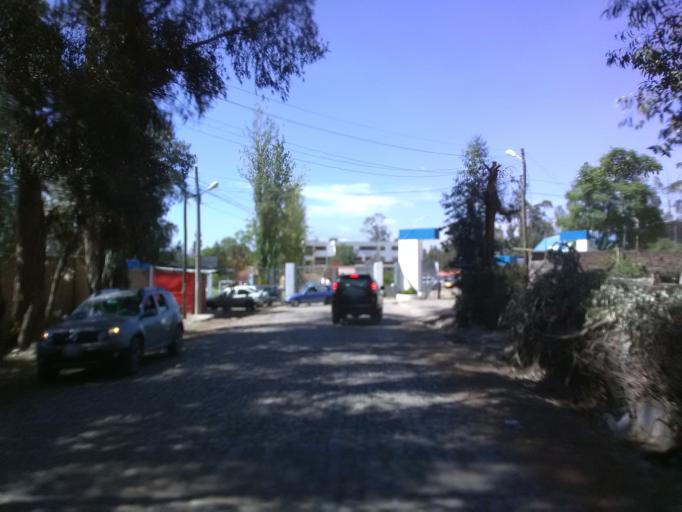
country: BO
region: Cochabamba
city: Cochabamba
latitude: -17.3542
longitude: -66.2015
